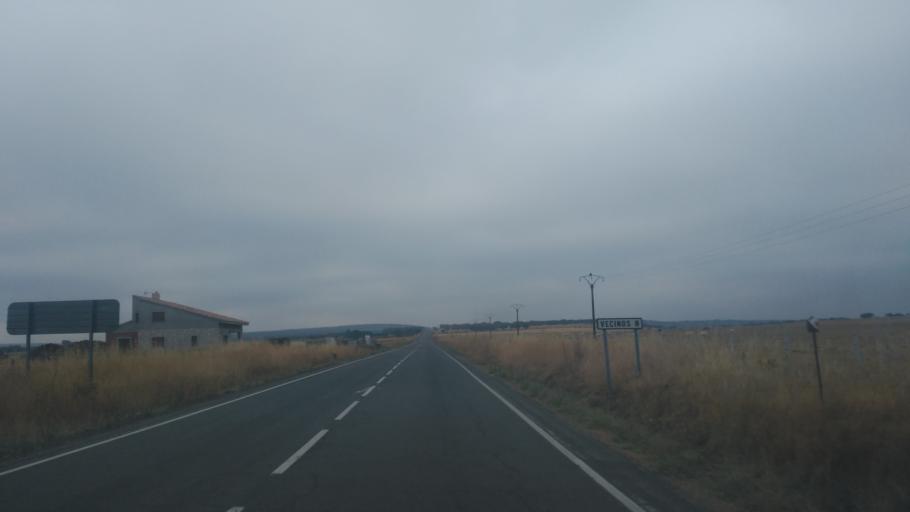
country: ES
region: Castille and Leon
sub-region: Provincia de Salamanca
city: Matilla de los Canos del Rio
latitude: 40.8223
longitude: -5.9426
